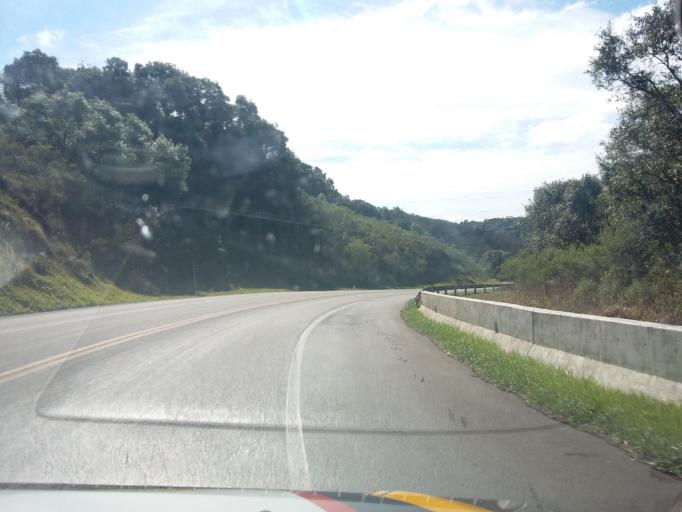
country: BR
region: Rio Grande do Sul
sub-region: Vacaria
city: Vacaria
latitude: -28.5932
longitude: -51.0297
